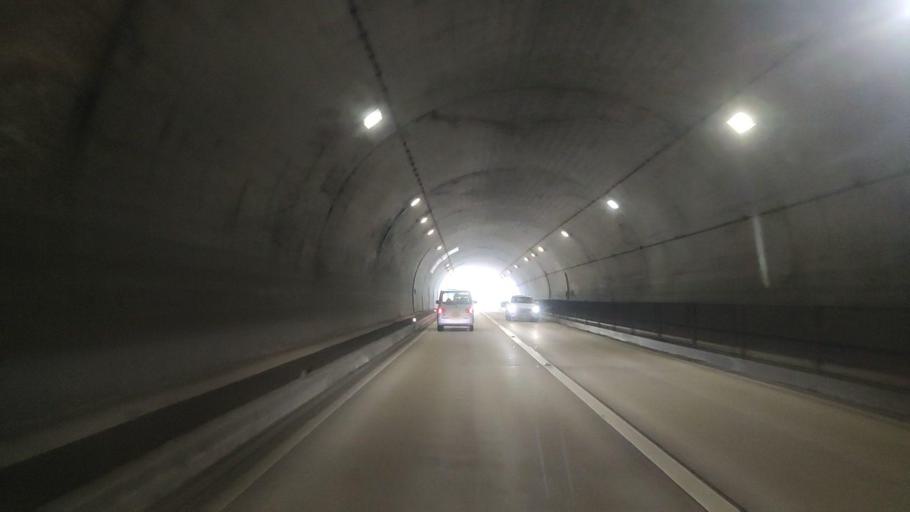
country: JP
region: Wakayama
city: Tanabe
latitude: 33.7140
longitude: 135.4529
